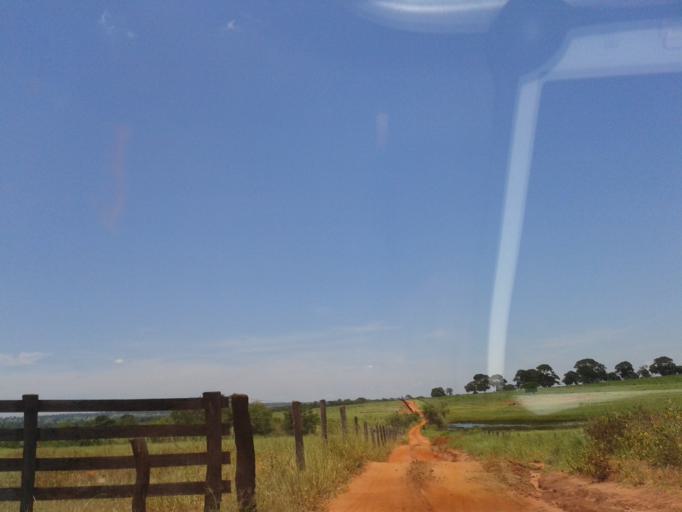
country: BR
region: Minas Gerais
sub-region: Santa Vitoria
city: Santa Vitoria
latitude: -19.2096
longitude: -50.4013
